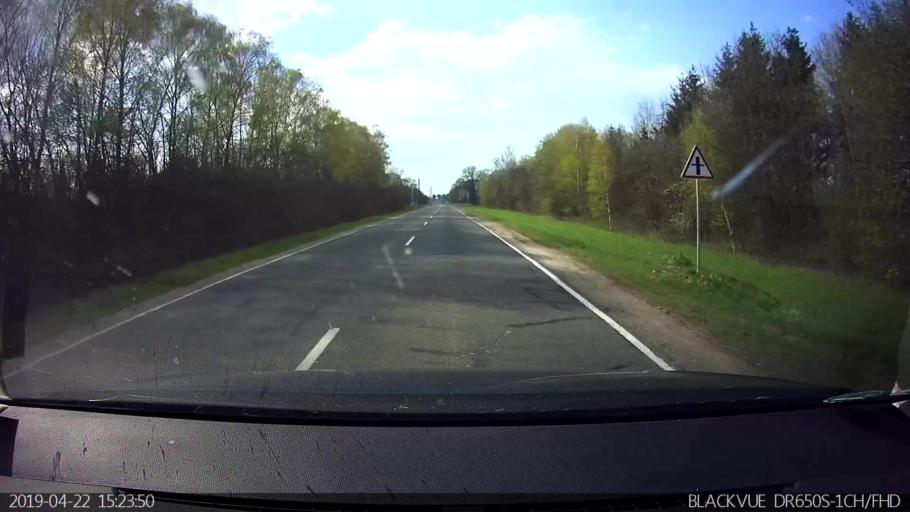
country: BY
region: Brest
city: Vysokaye
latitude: 52.3577
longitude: 23.4184
